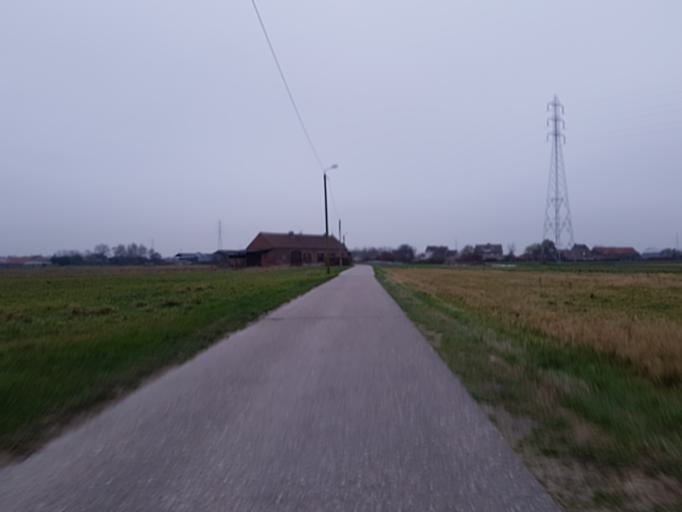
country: BE
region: Flanders
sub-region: Provincie Antwerpen
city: Rumst
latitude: 51.0292
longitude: 4.4128
